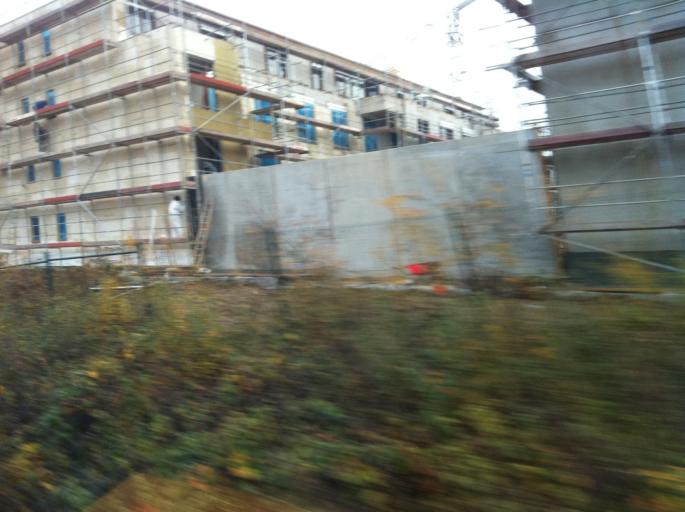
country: LU
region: Luxembourg
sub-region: Canton d'Esch-sur-Alzette
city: Schifflange
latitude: 49.5099
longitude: 6.0257
